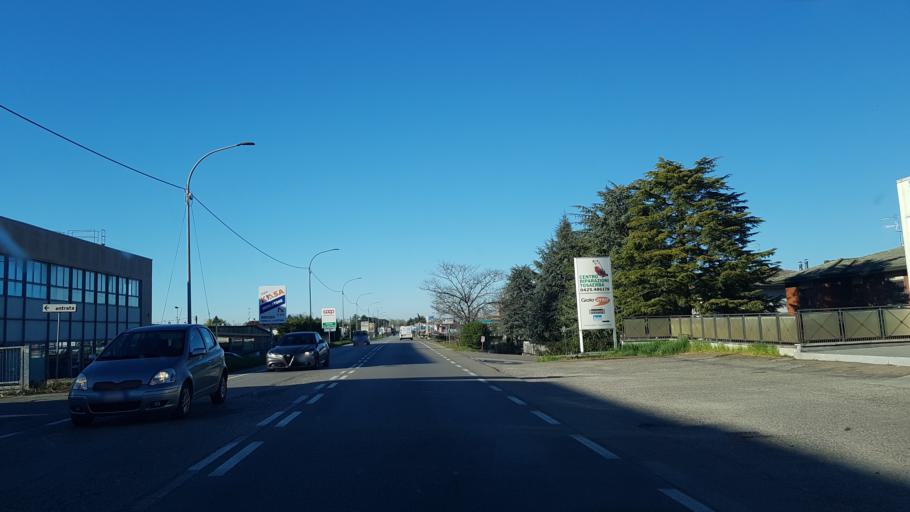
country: IT
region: Veneto
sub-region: Provincia di Padova
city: Boara Pisani
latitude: 45.0965
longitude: 11.7856
